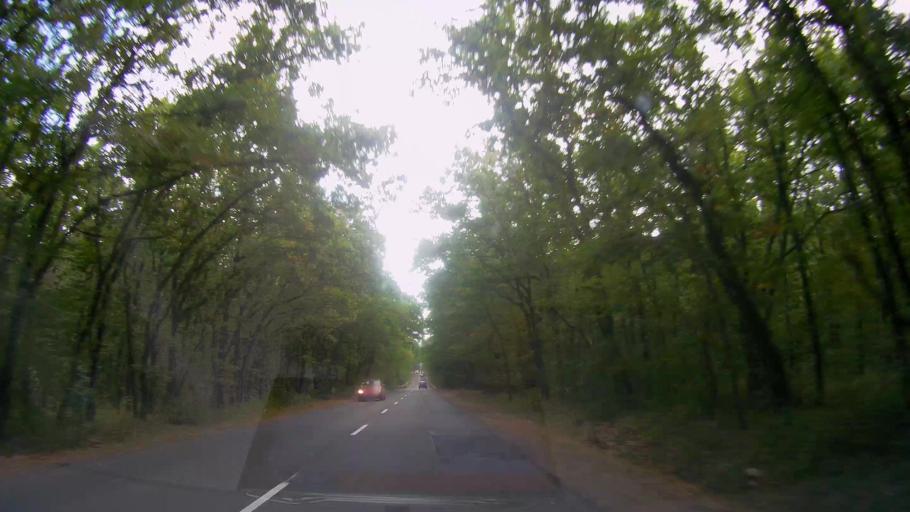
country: BG
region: Burgas
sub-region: Obshtina Primorsko
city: Primorsko
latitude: 42.2877
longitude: 27.7356
